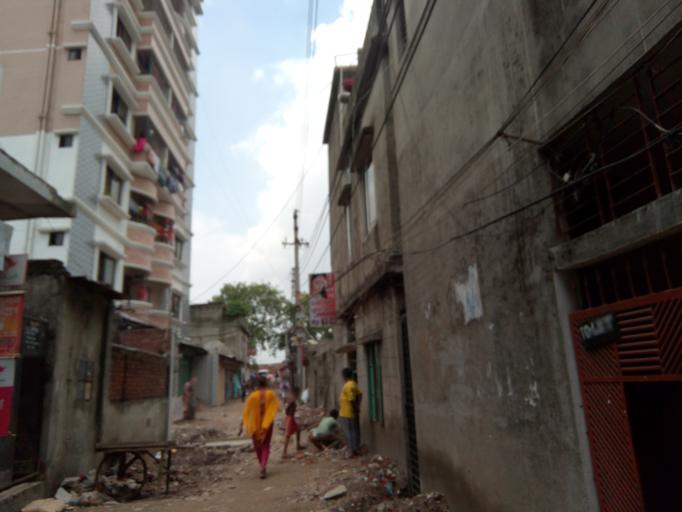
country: BD
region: Dhaka
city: Azimpur
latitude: 23.7498
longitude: 90.3591
